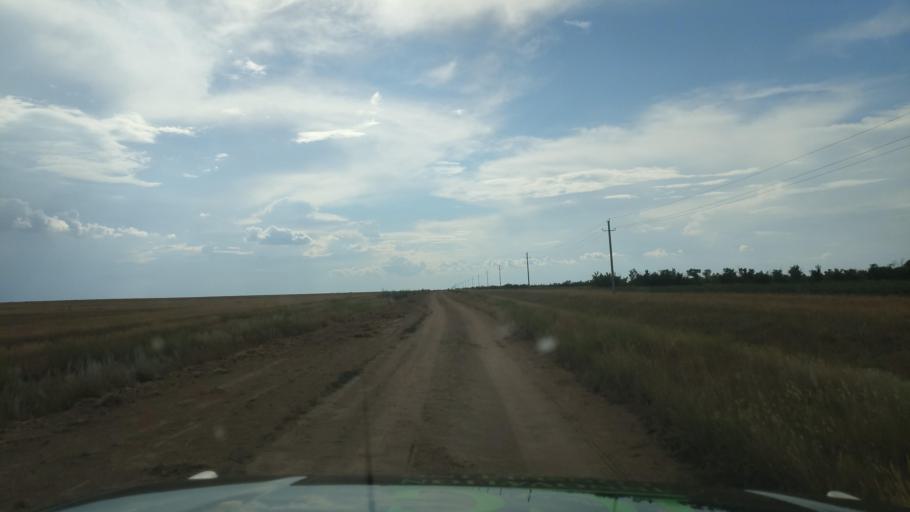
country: KZ
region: Pavlodar
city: Pavlodar
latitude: 52.5124
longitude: 77.5167
